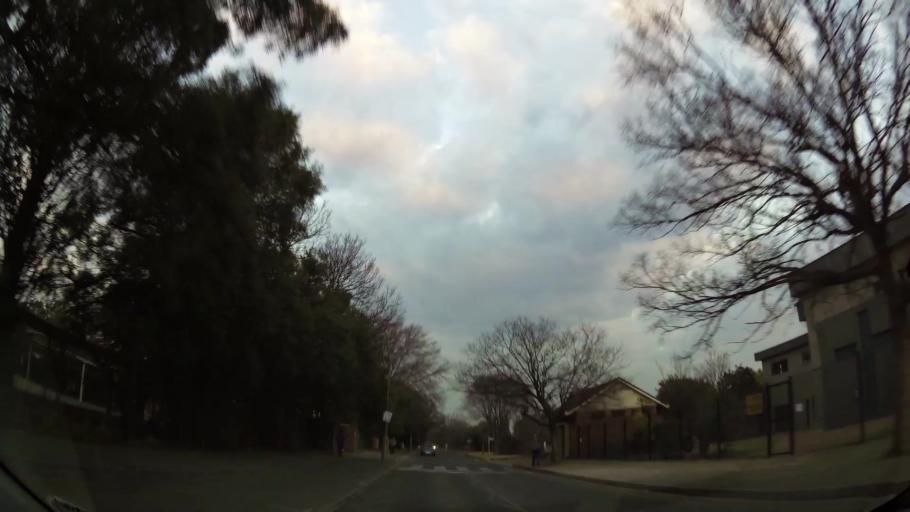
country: ZA
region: Gauteng
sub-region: Ekurhuleni Metropolitan Municipality
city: Benoni
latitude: -26.1755
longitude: 28.3079
